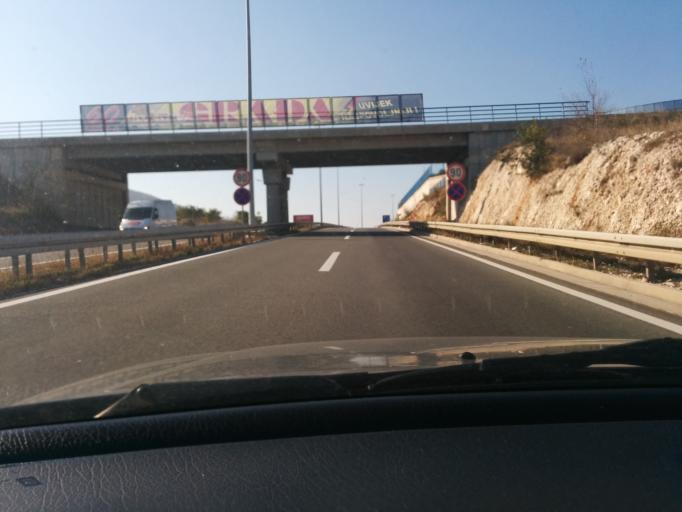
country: HR
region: Splitsko-Dalmatinska
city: Dugopolje
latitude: 43.5852
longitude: 16.5641
